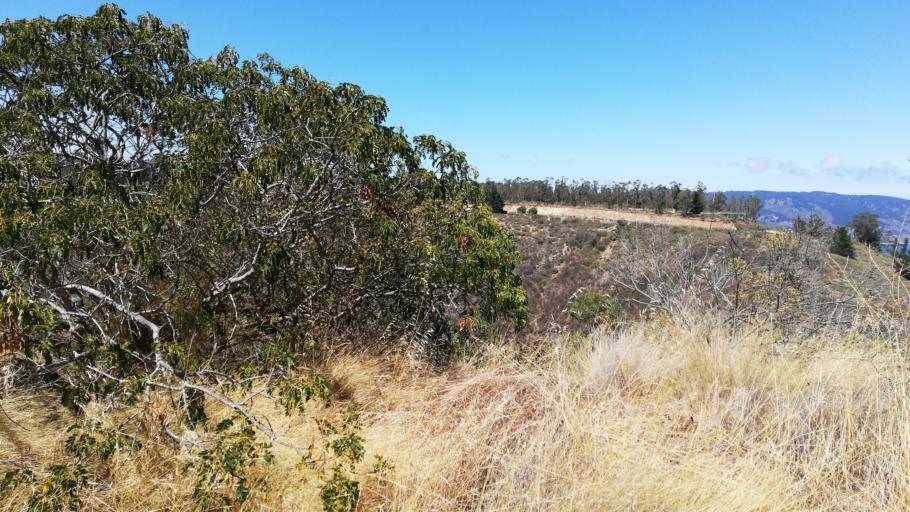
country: CL
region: Valparaiso
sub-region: Provincia de Valparaiso
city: Valparaiso
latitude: -33.0766
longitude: -71.6570
